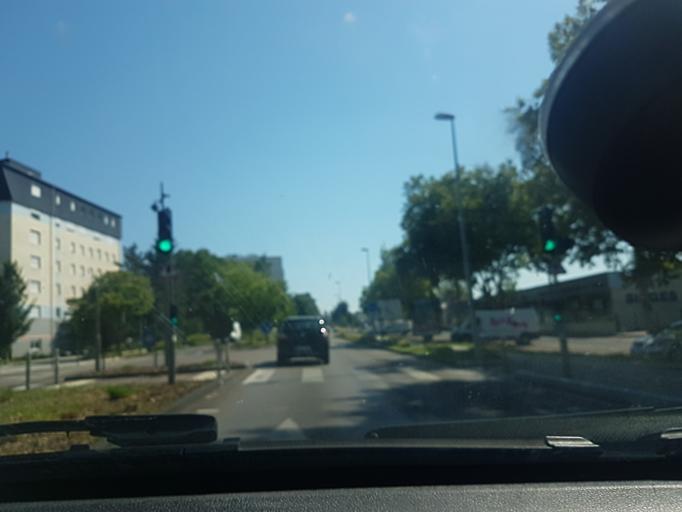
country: FR
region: Bourgogne
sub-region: Departement de Saone-et-Loire
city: Chalon-sur-Saone
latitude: 46.7924
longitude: 4.8634
